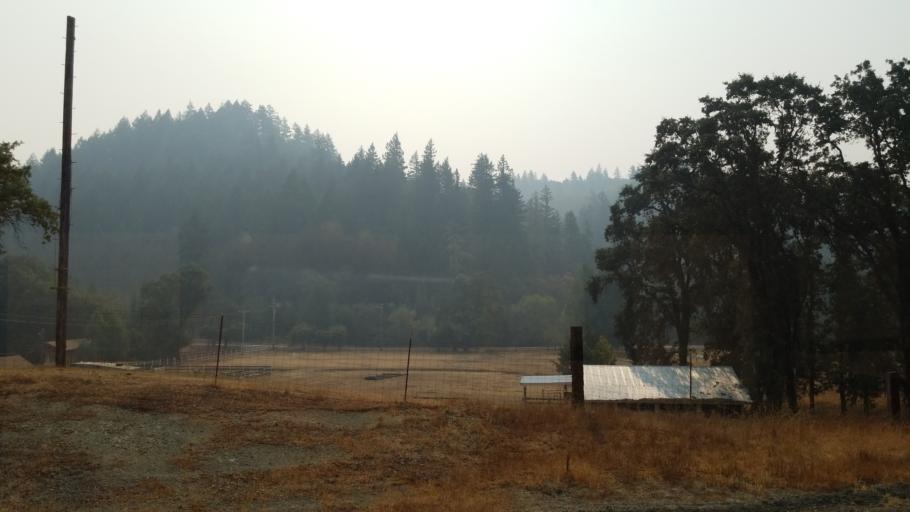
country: US
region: California
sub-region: Mendocino County
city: Willits
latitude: 39.4054
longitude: -123.3885
